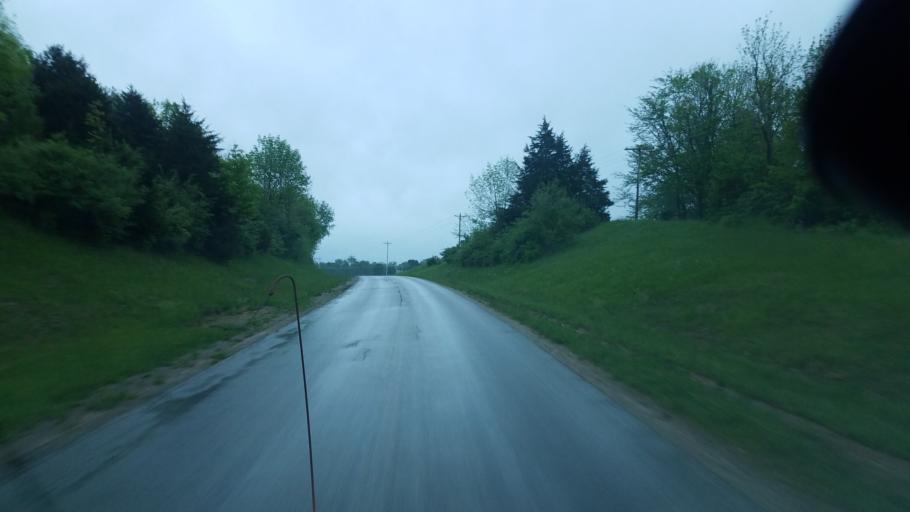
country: US
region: Ohio
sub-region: Highland County
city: Greenfield
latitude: 39.2903
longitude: -83.4610
